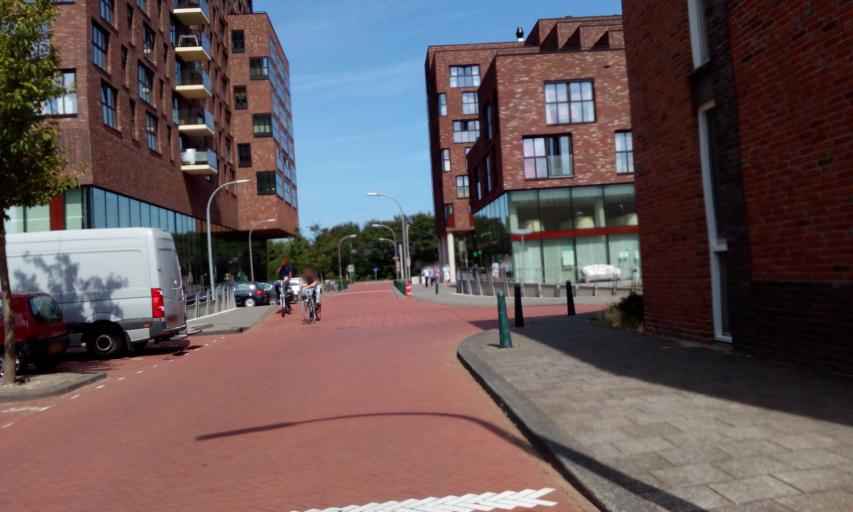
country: NL
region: South Holland
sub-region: Gemeente Den Haag
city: Ypenburg
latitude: 52.0528
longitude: 4.3874
